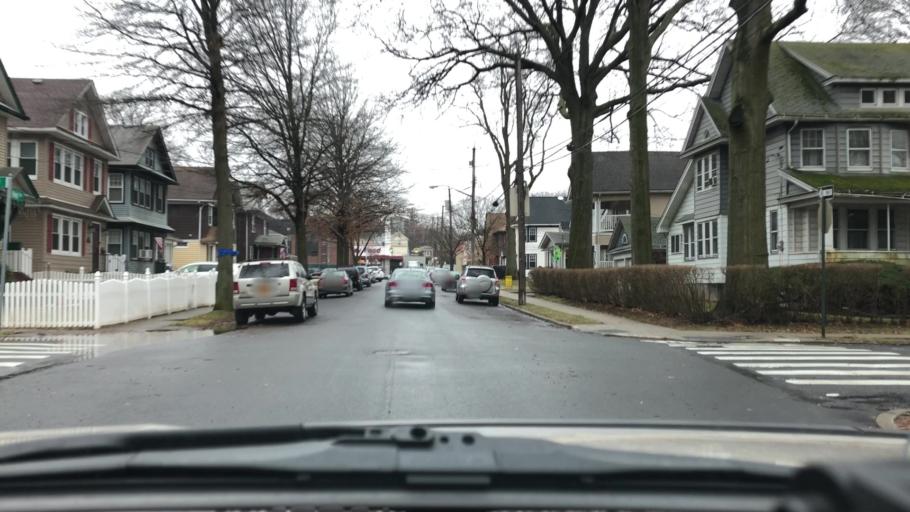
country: US
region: New Jersey
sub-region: Hudson County
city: Bayonne
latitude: 40.6322
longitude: -74.1051
